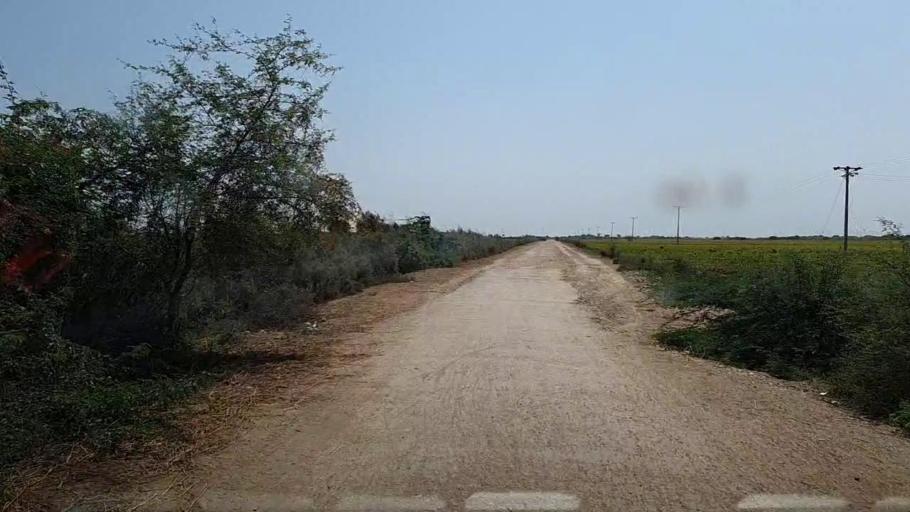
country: PK
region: Sindh
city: Mirpur Batoro
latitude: 24.6403
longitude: 68.4522
